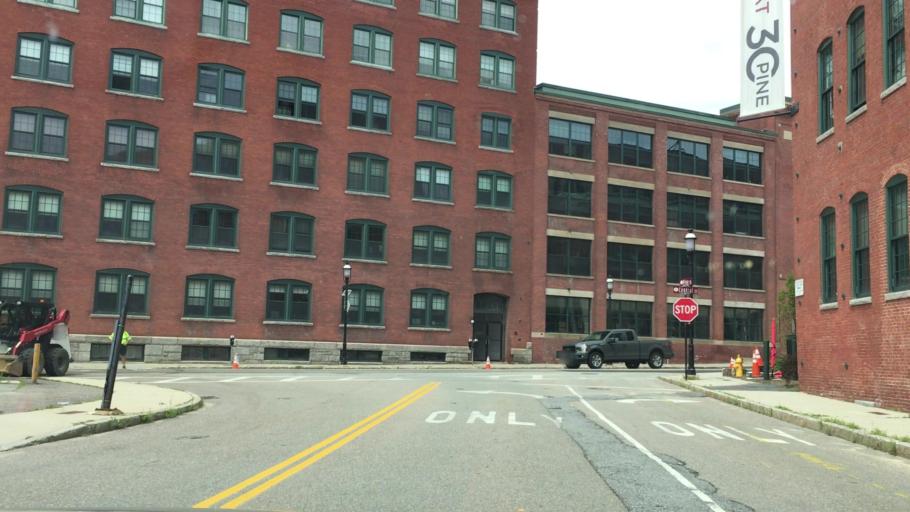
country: US
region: Massachusetts
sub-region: Worcester County
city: Gardner
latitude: 42.5771
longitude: -71.9934
